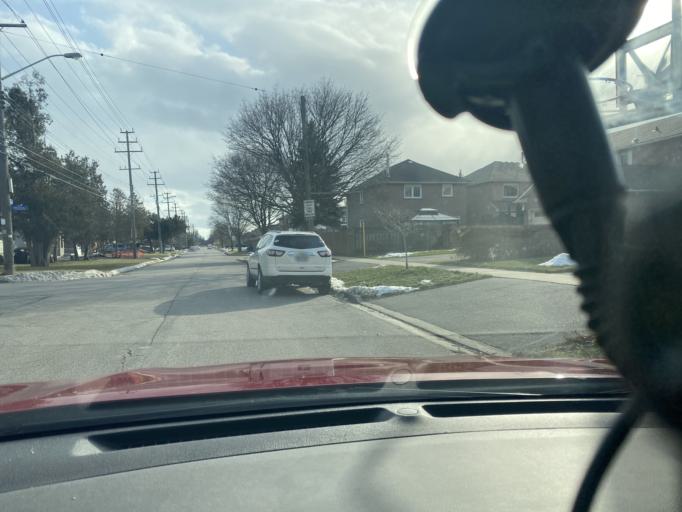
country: CA
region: Ontario
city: Scarborough
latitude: 43.7972
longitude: -79.1764
